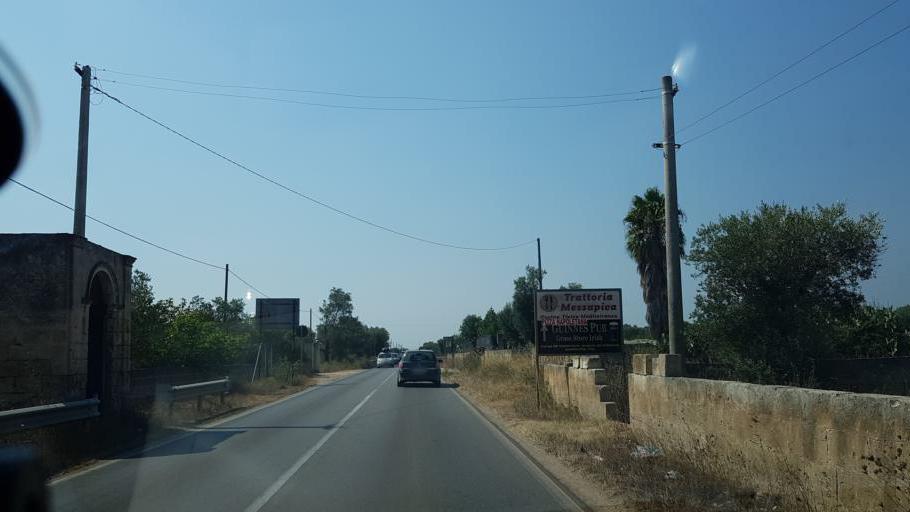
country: IT
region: Apulia
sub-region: Provincia di Taranto
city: Manduria
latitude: 40.4206
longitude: 17.6326
